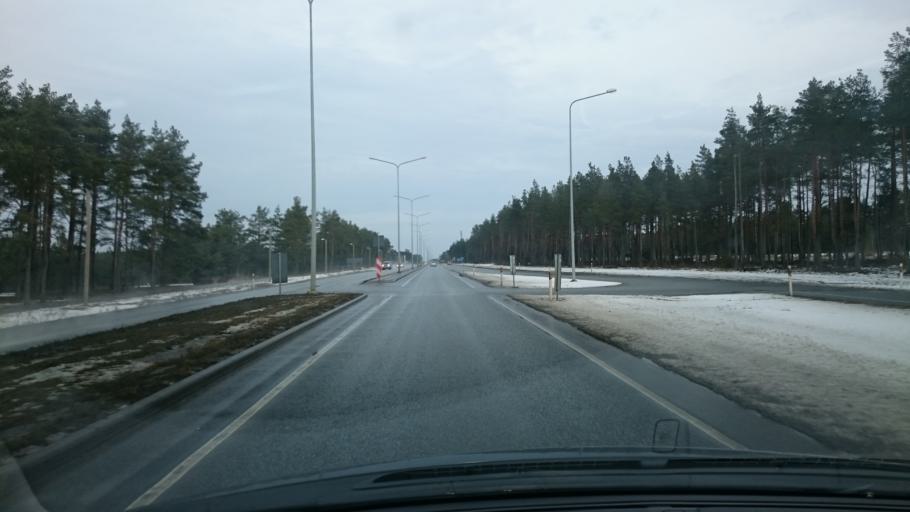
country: EE
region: Harju
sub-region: Saku vald
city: Saku
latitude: 59.3317
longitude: 24.6955
